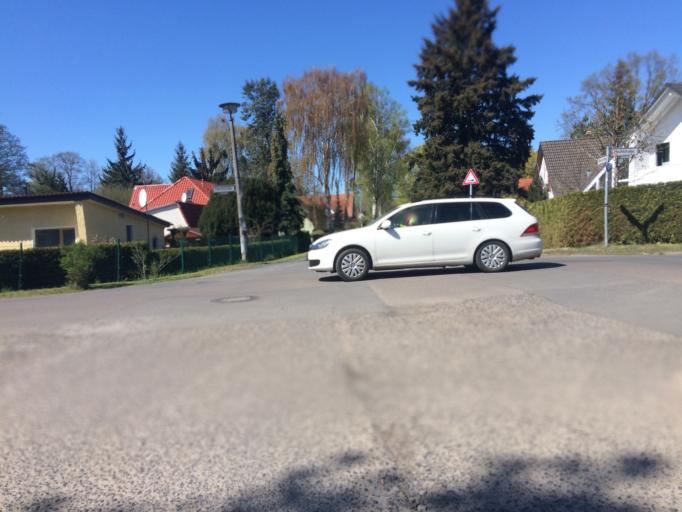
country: DE
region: Berlin
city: Rahnsdorf
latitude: 52.4359
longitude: 13.6887
